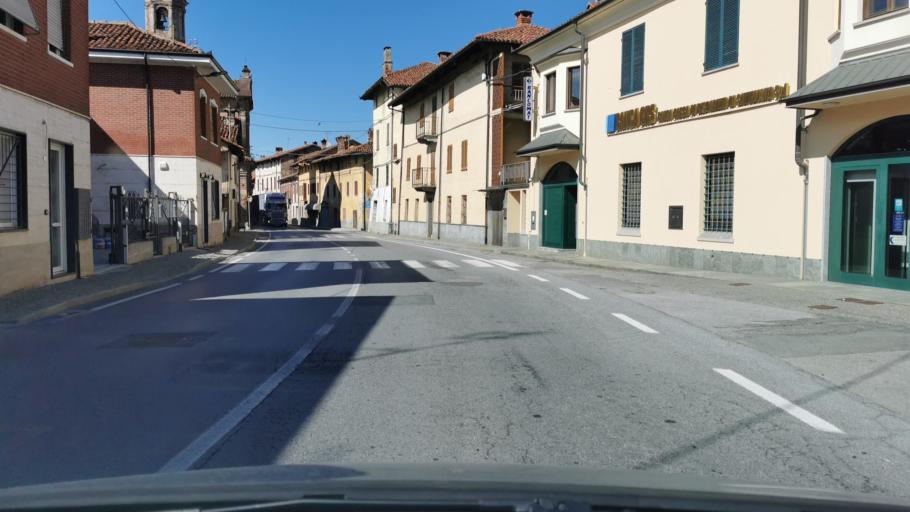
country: IT
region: Piedmont
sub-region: Provincia di Cuneo
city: Vottignasco
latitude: 44.5558
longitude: 7.6219
